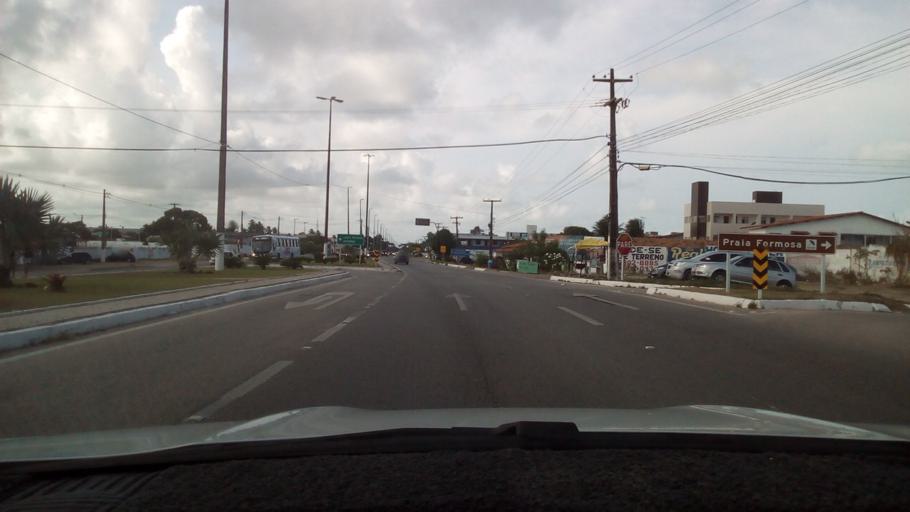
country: BR
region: Paraiba
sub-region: Cabedelo
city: Cabedelo
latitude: -6.9848
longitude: -34.8290
